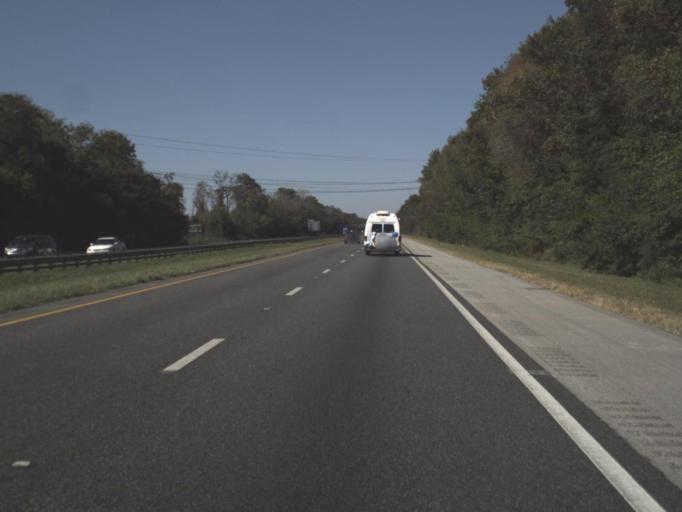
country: US
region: Florida
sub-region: Sumter County
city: Wildwood
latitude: 28.8428
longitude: -82.0615
